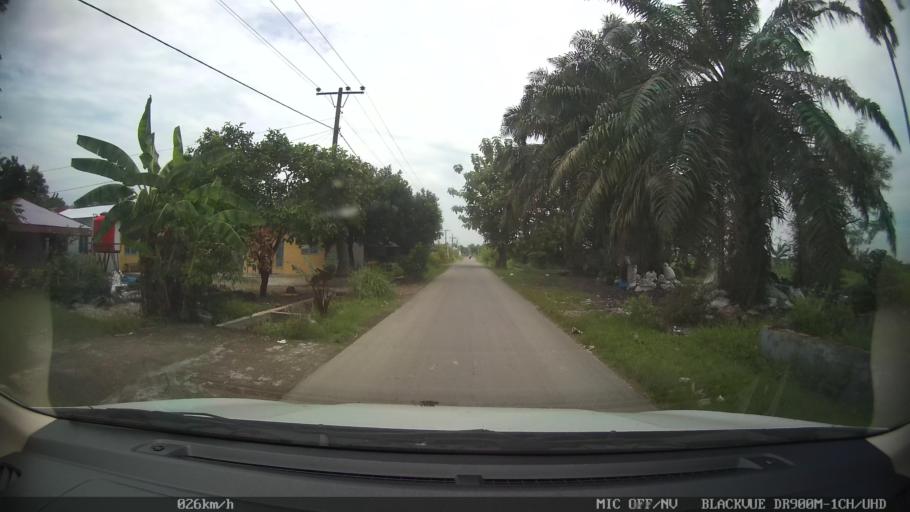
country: ID
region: North Sumatra
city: Sunggal
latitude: 3.6340
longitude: 98.5700
